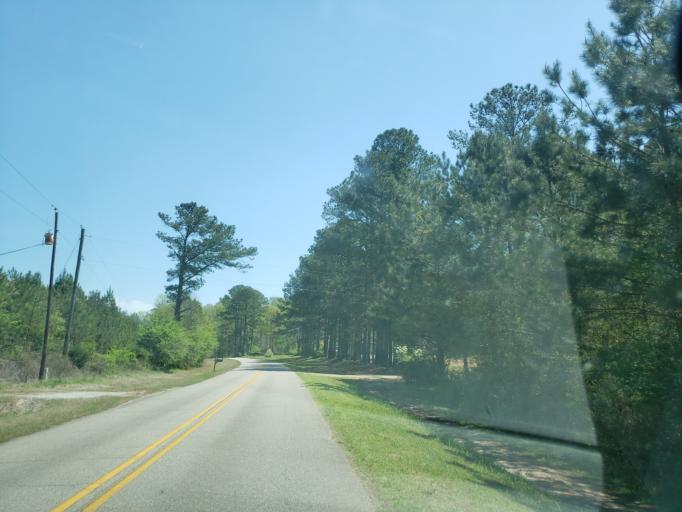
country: US
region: Alabama
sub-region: Tallapoosa County
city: Camp Hill
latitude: 32.6863
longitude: -85.6802
